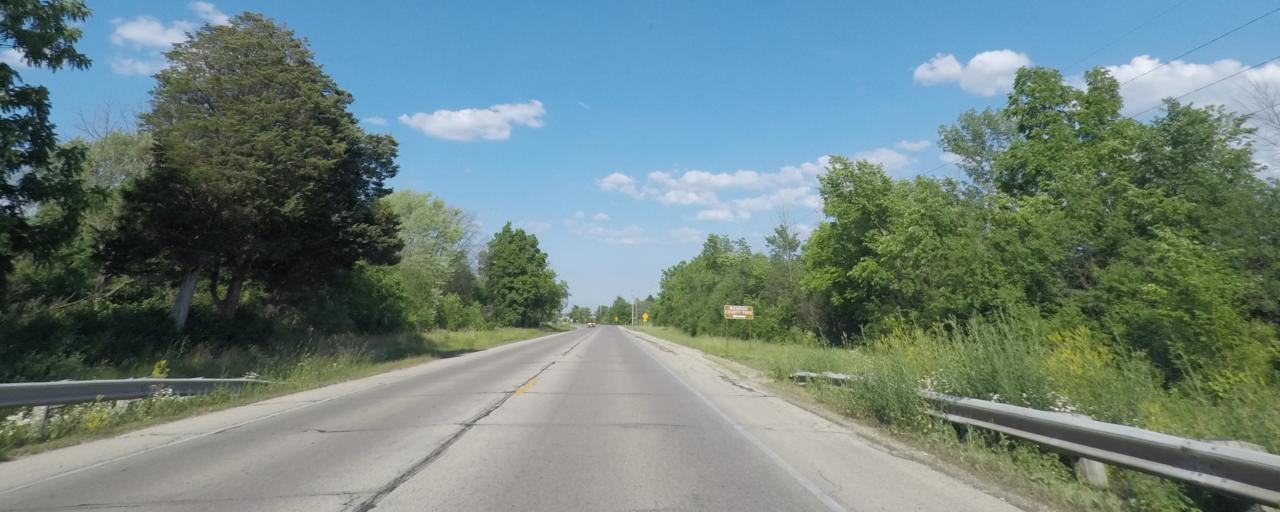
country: US
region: Wisconsin
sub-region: Waukesha County
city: Muskego
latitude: 42.8935
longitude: -88.1676
